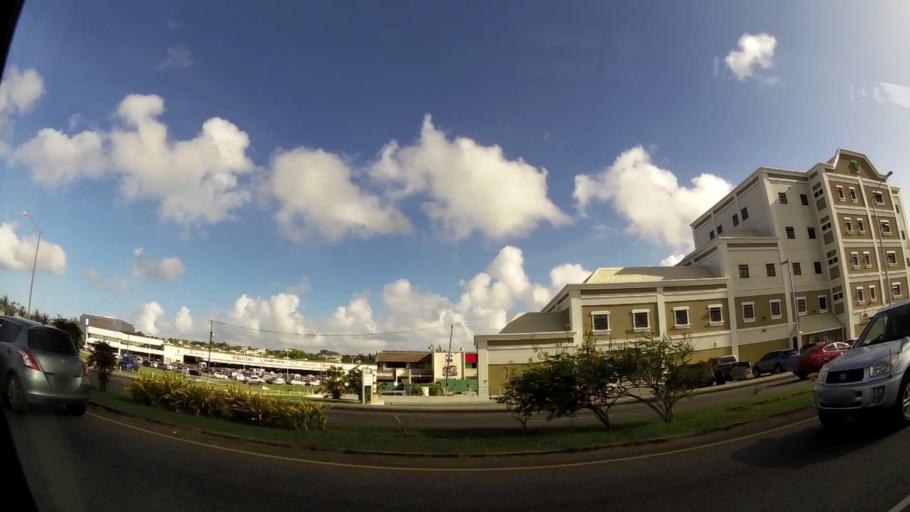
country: BB
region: Saint Michael
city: Bridgetown
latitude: 13.1424
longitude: -59.6084
